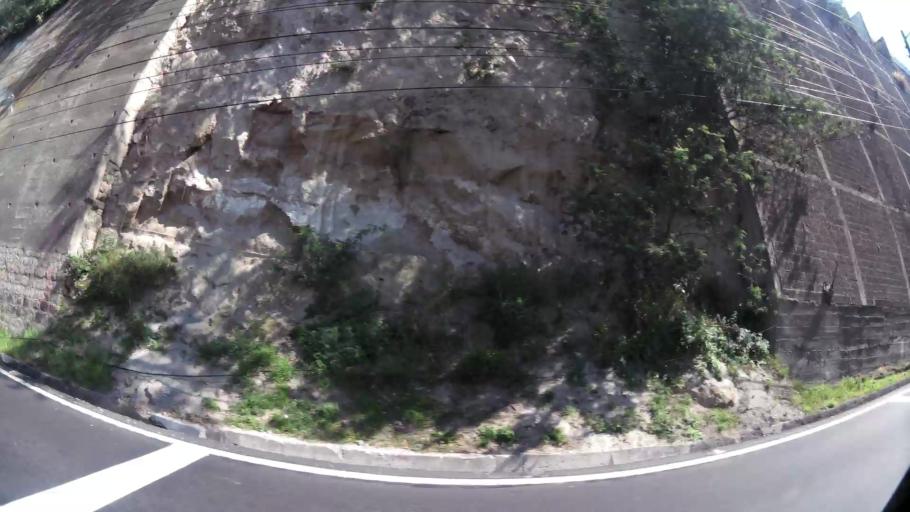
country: EC
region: Pichincha
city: Quito
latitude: -0.1910
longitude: -78.4426
